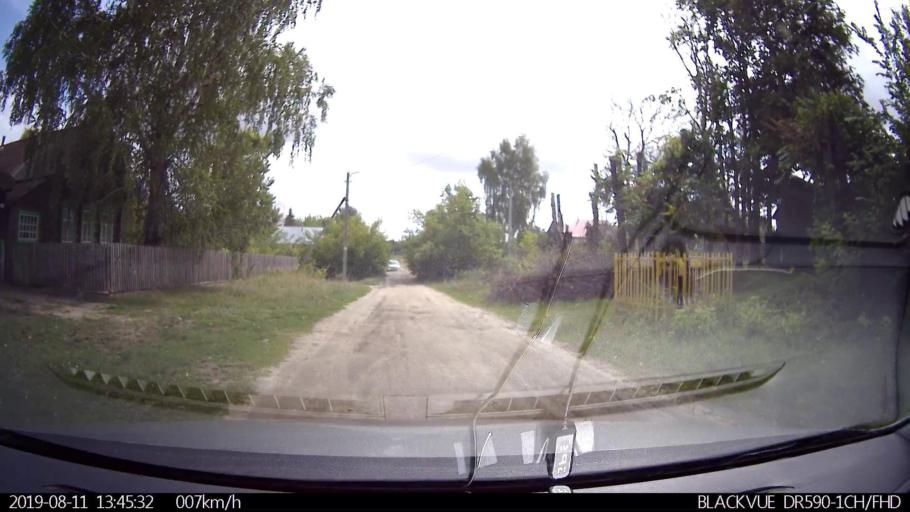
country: RU
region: Ulyanovsk
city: Ignatovka
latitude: 53.8521
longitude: 47.5747
